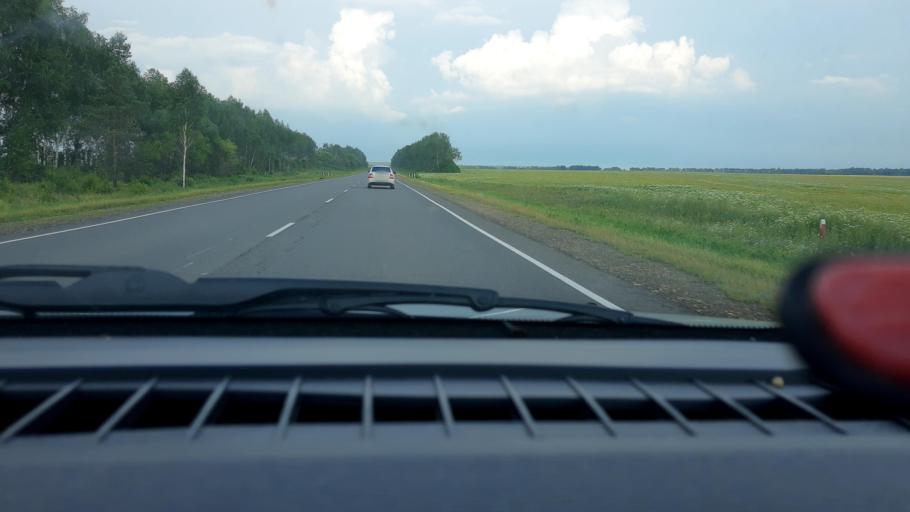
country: RU
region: Nizjnij Novgorod
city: Shatki
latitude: 55.2435
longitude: 44.0192
